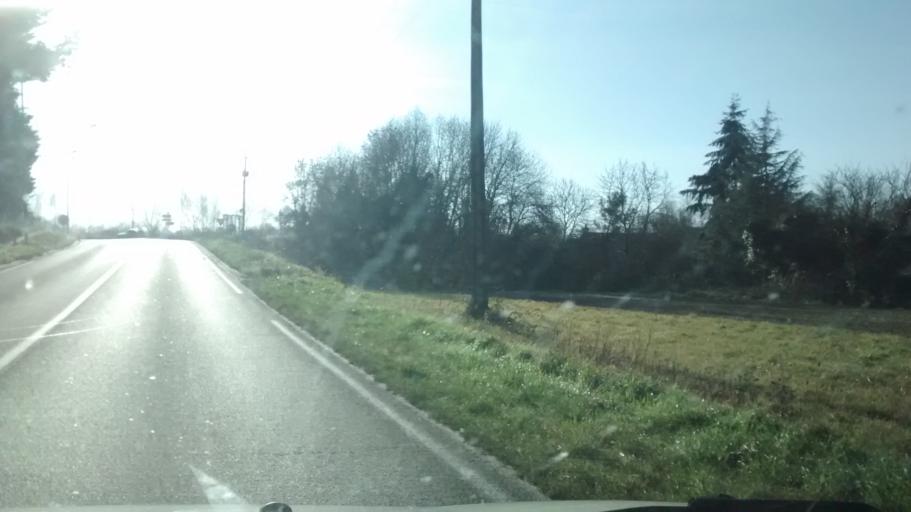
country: FR
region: Centre
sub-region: Departement d'Indre-et-Loire
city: Amboise
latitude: 47.4141
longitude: 0.9631
